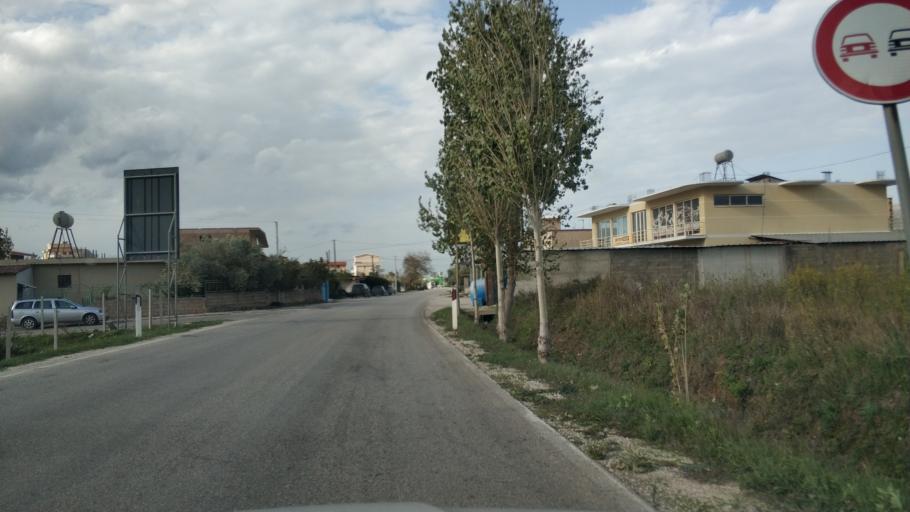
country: AL
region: Vlore
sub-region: Rrethi i Vlores
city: Orikum
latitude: 40.3263
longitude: 19.4789
